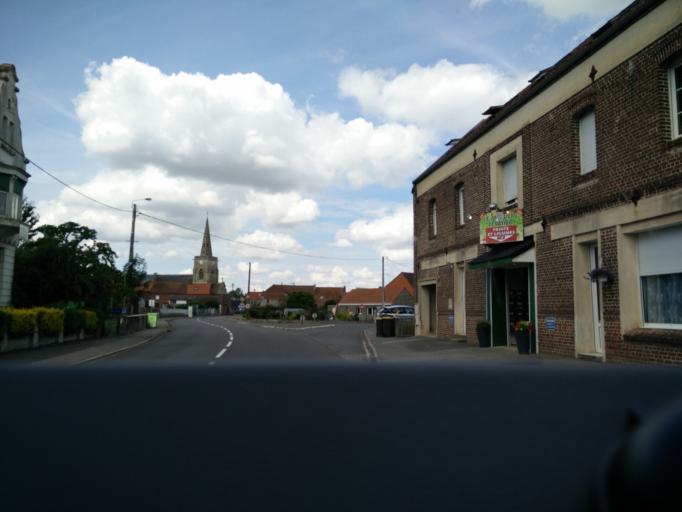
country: FR
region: Nord-Pas-de-Calais
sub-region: Departement du Pas-de-Calais
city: Robecq
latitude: 50.5945
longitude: 2.5665
